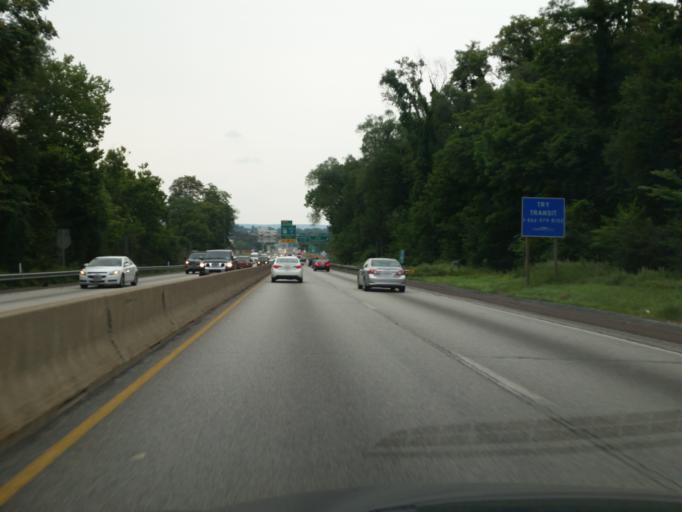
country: US
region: Pennsylvania
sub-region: Cumberland County
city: New Cumberland
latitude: 40.2253
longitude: -76.8872
